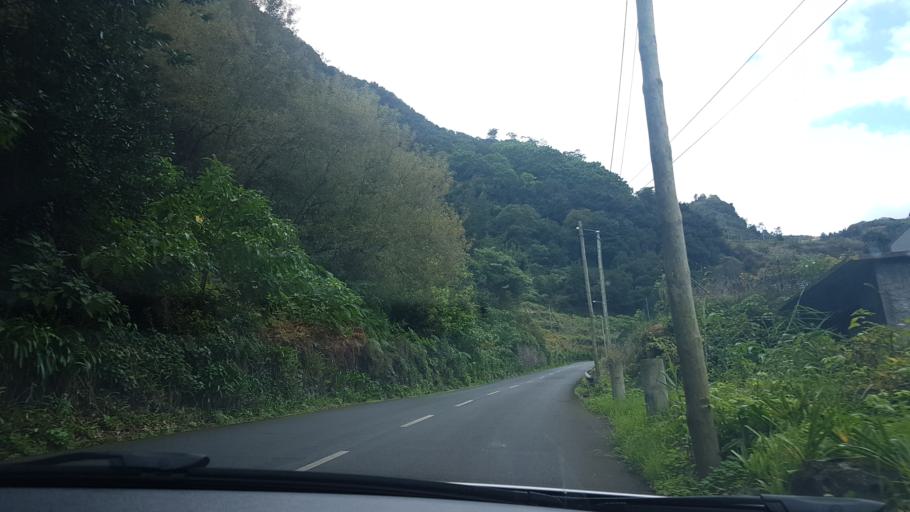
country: PT
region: Madeira
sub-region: Santana
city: Santana
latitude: 32.8159
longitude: -16.8990
